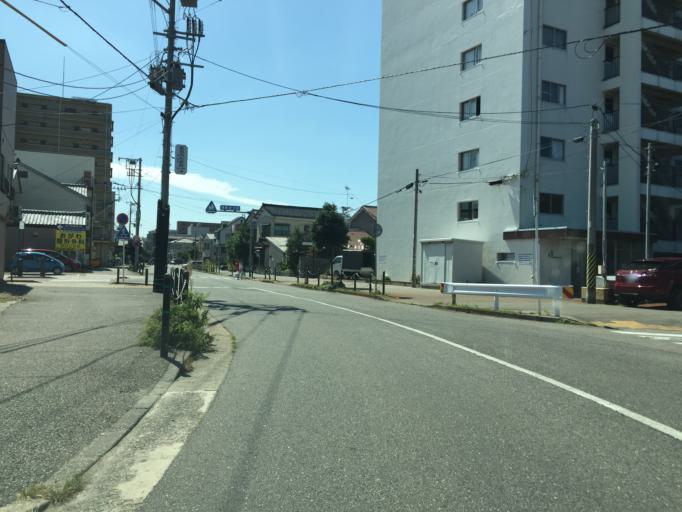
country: JP
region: Niigata
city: Niigata-shi
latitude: 37.9301
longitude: 139.0501
